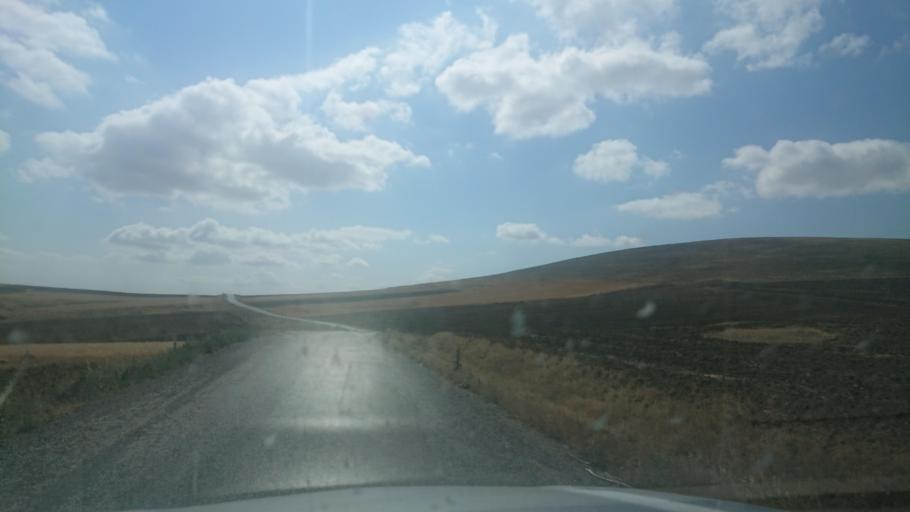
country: TR
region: Aksaray
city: Sariyahsi
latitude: 39.0032
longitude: 33.9634
